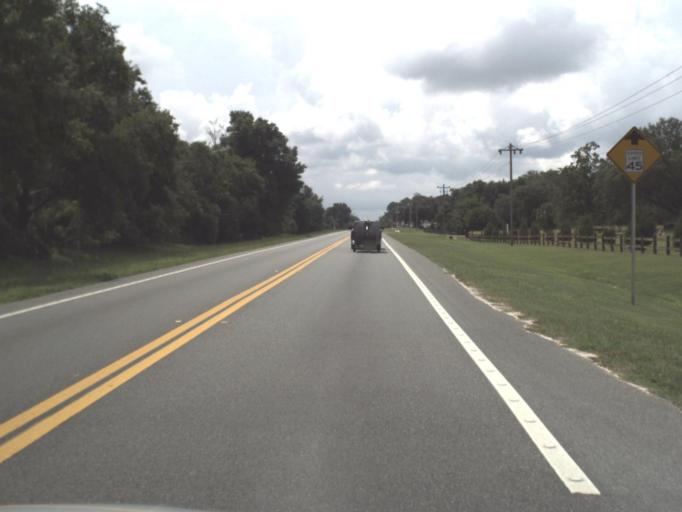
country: US
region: Florida
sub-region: Clay County
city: Keystone Heights
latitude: 29.7950
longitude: -82.0464
